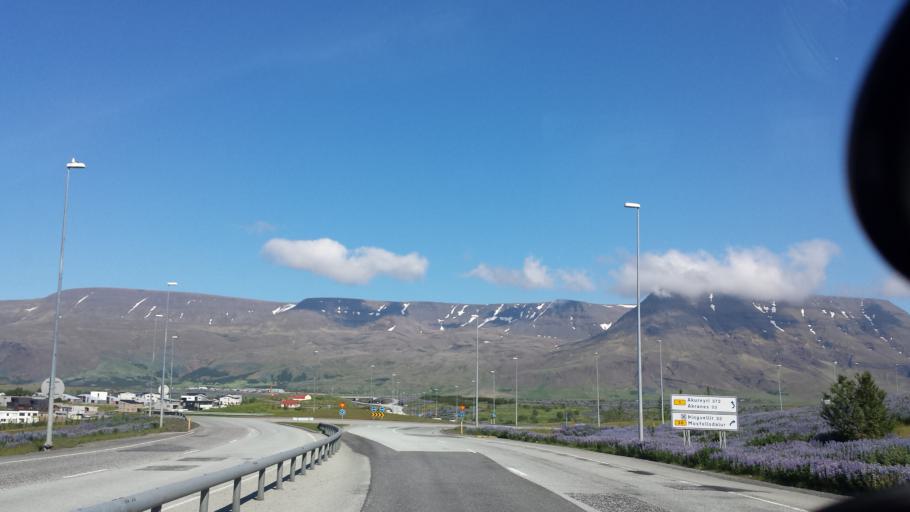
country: IS
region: Capital Region
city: Mosfellsbaer
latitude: 64.1748
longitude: -21.6764
